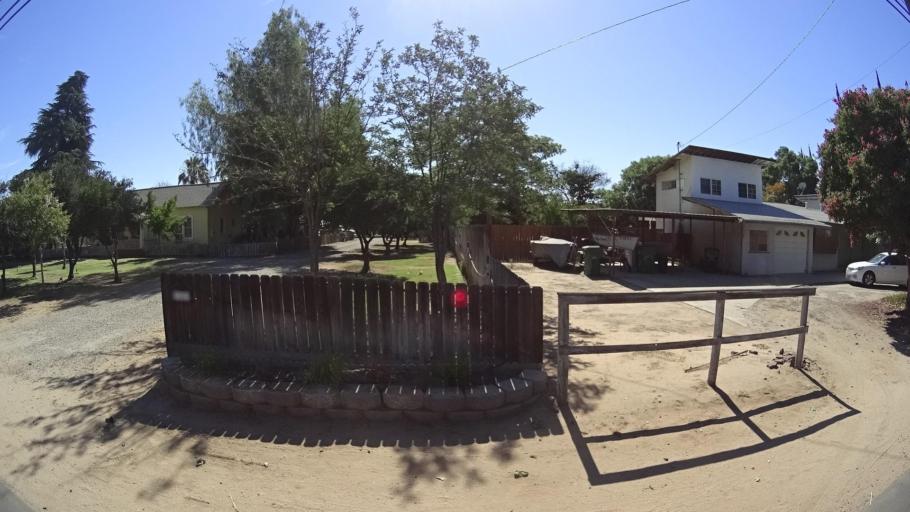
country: US
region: California
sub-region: Fresno County
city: Sunnyside
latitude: 36.7443
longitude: -119.7092
